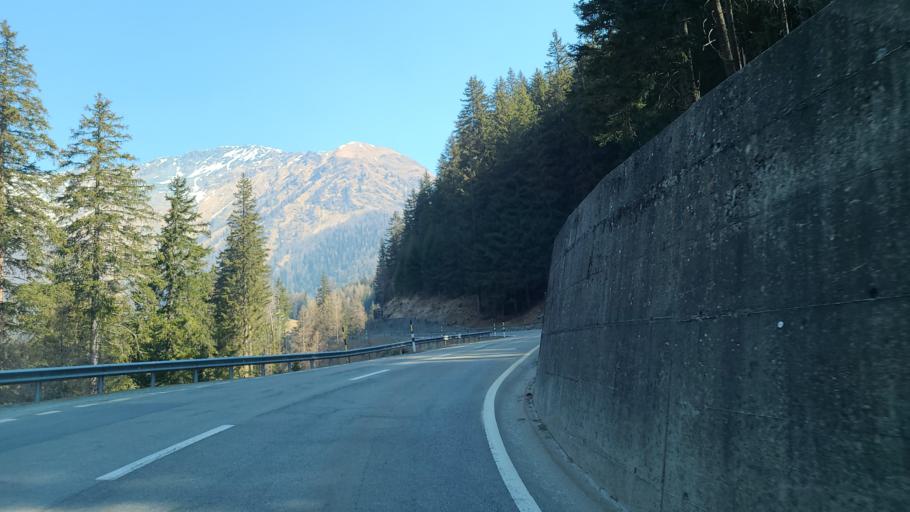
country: CH
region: Grisons
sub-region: Bernina District
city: Poschiavo
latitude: 46.3773
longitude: 10.0698
